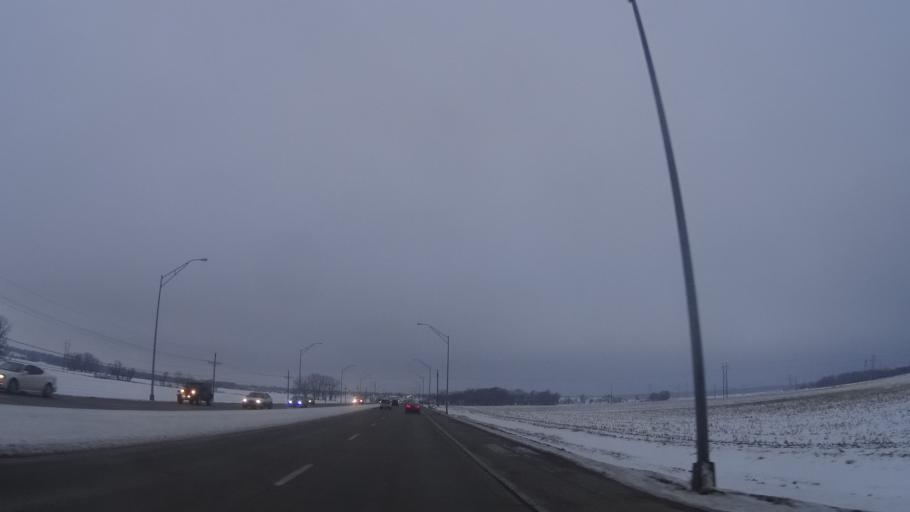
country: US
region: Nebraska
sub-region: Sarpy County
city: La Vista
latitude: 41.1619
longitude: -95.9722
